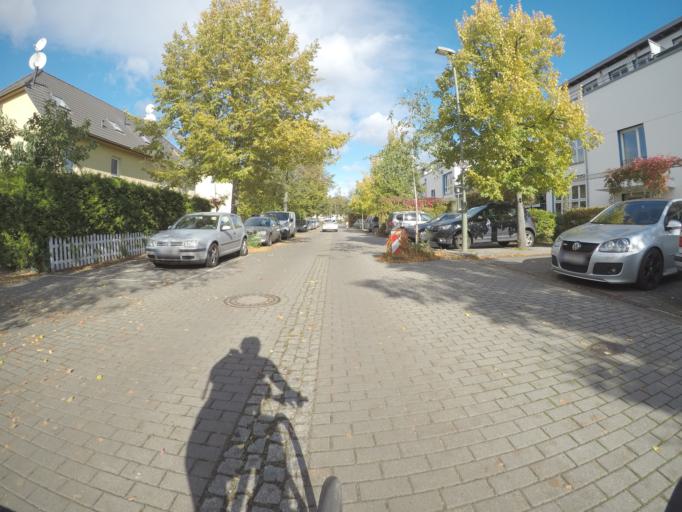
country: DE
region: Berlin
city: Staaken
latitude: 52.5283
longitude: 13.1399
